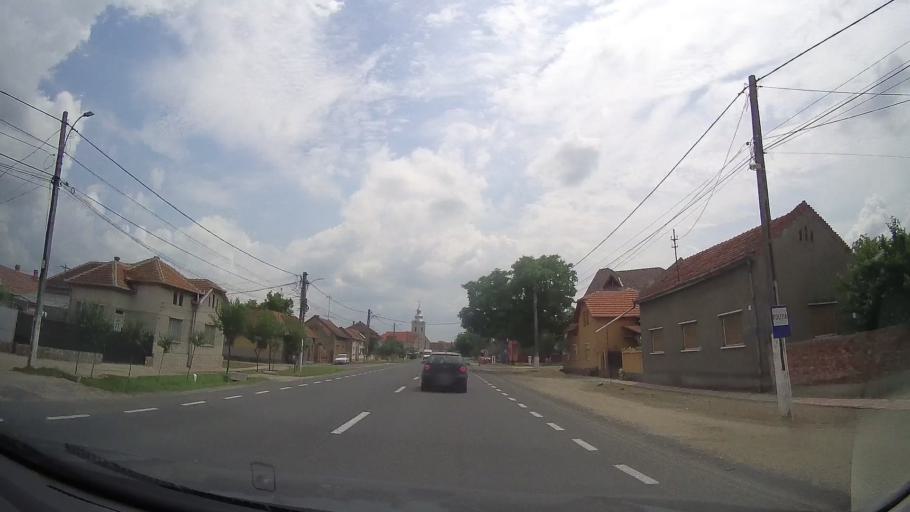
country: RO
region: Timis
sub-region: Comuna Costeiu
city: Costeiu
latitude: 45.7334
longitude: 21.8636
